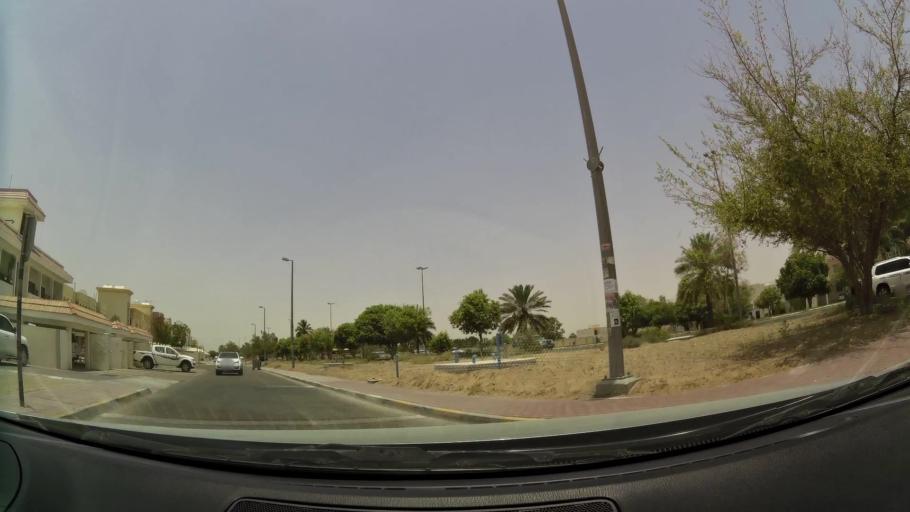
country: AE
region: Abu Dhabi
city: Al Ain
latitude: 24.2122
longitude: 55.7416
